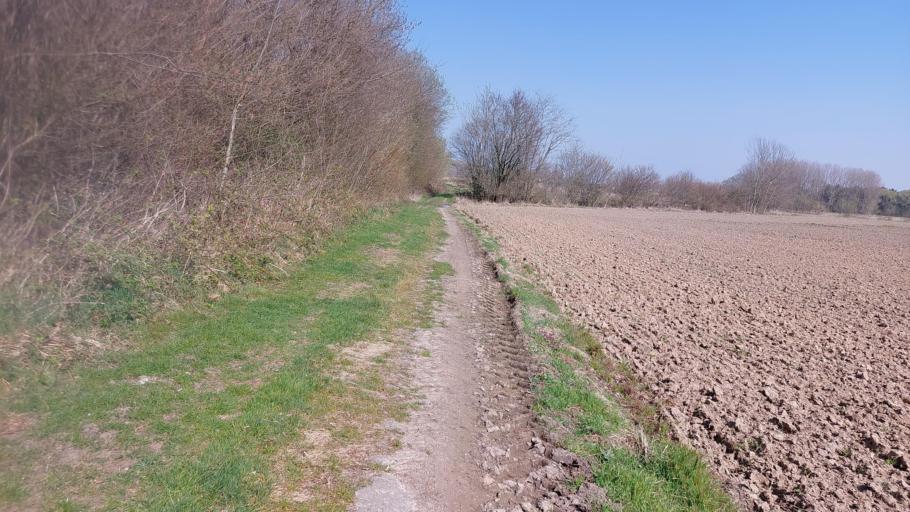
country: BE
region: Wallonia
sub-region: Province du Hainaut
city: Soignies
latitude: 50.5290
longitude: 4.0169
